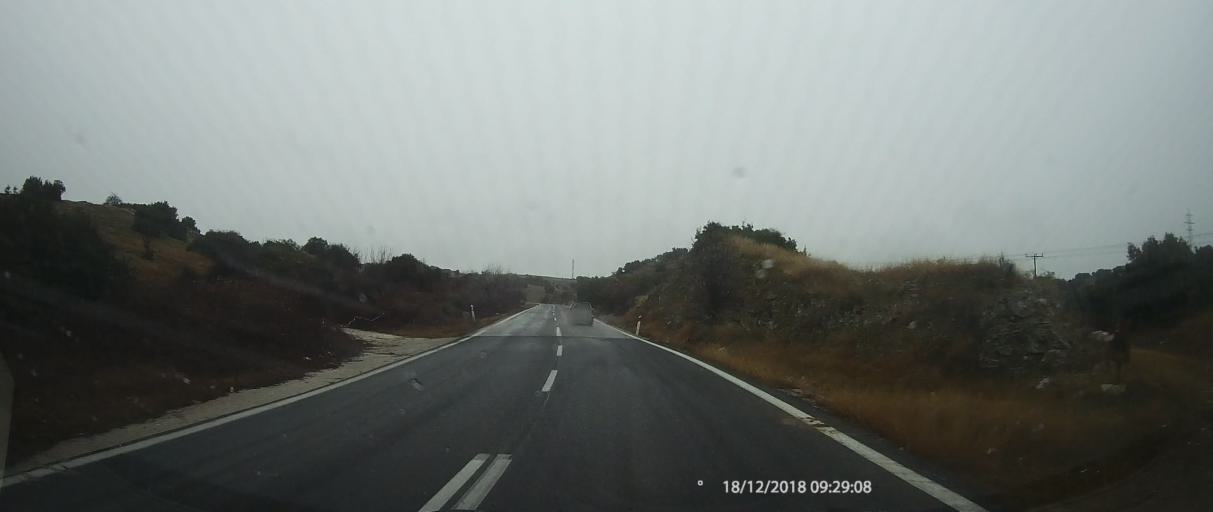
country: GR
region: Thessaly
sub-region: Nomos Larisis
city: Elassona
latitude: 39.9251
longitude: 22.1715
